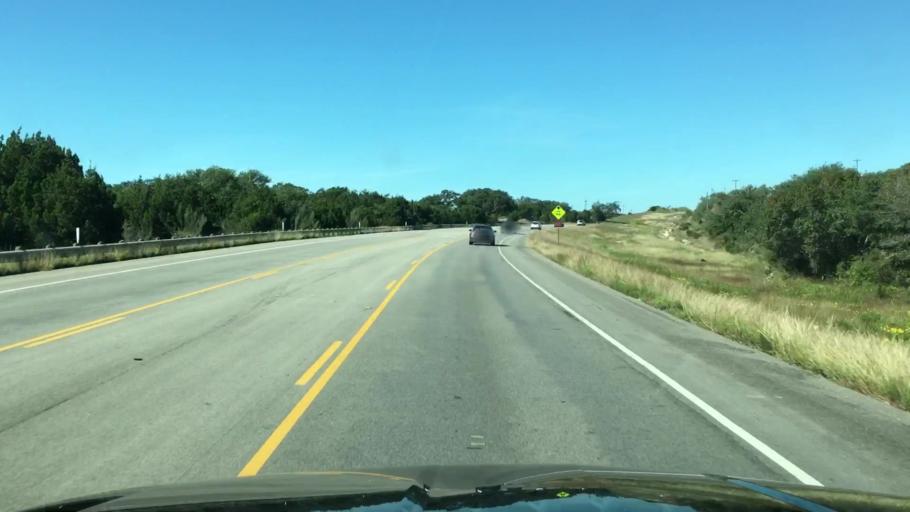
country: US
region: Texas
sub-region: Hays County
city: Dripping Springs
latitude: 30.1976
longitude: -98.1753
